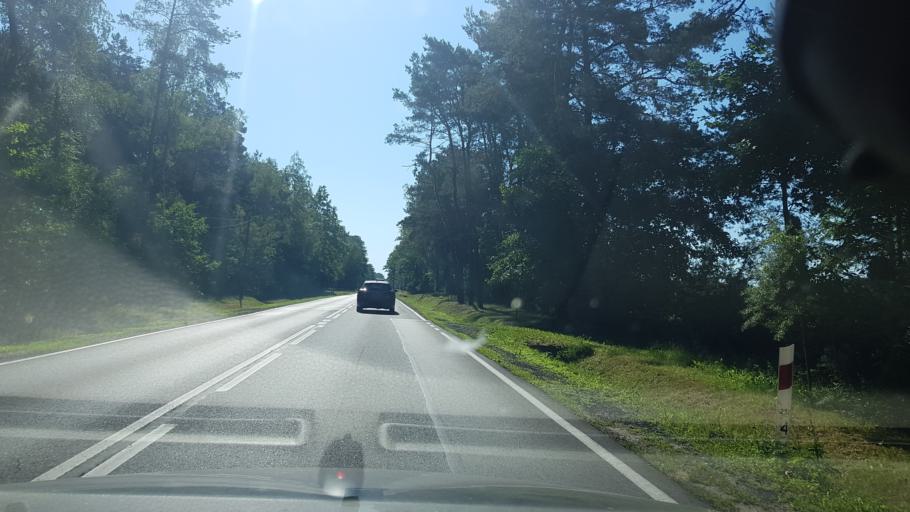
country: PL
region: Masovian Voivodeship
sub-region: Powiat wyszkowski
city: Branszczyk
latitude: 52.5538
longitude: 21.6047
